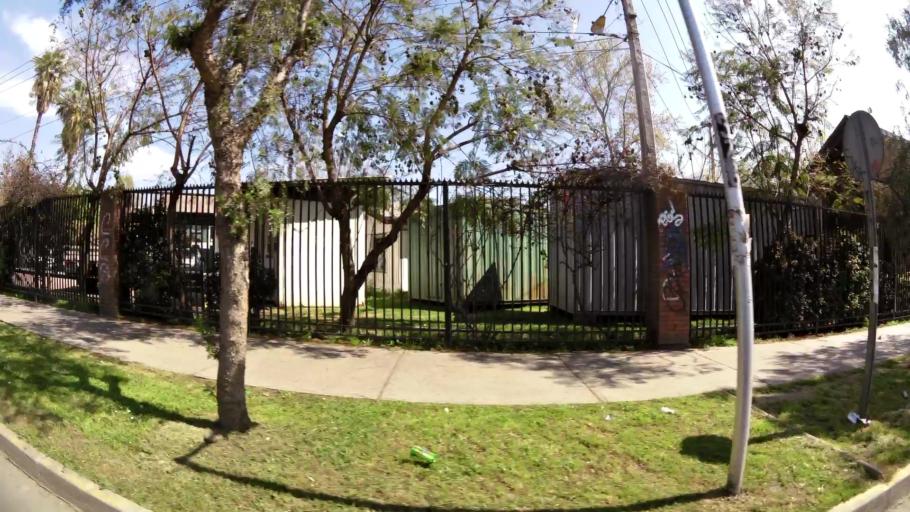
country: CL
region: Santiago Metropolitan
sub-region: Provincia de Santiago
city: Lo Prado
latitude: -33.4036
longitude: -70.7032
